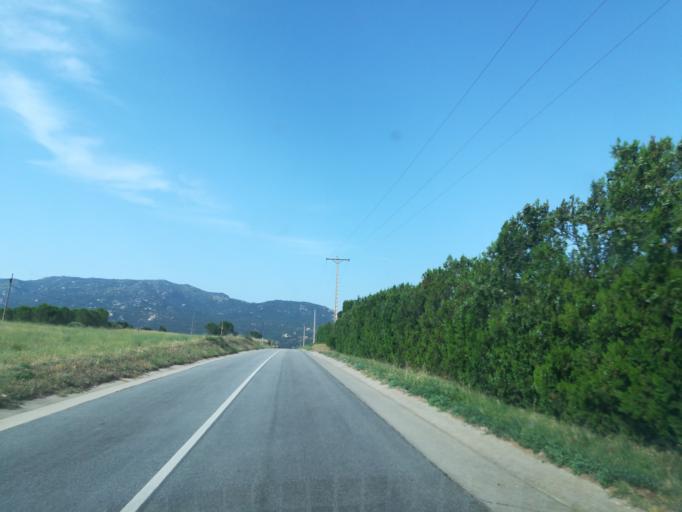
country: ES
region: Catalonia
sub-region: Provincia de Girona
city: Agullana
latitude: 42.3967
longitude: 2.8602
